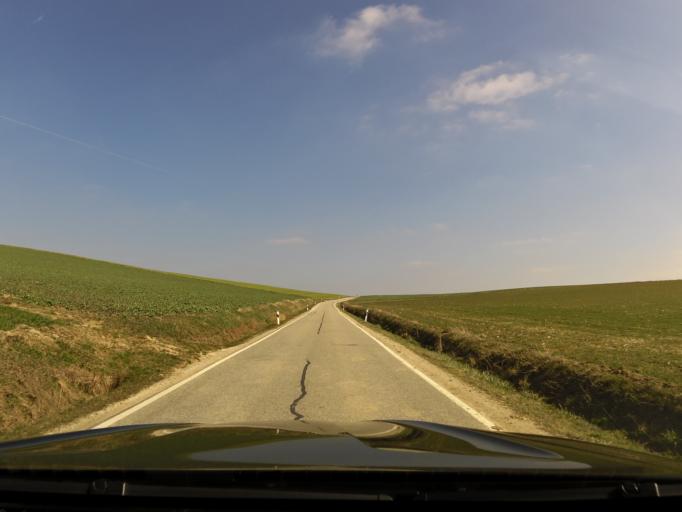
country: DE
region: Bavaria
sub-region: Lower Bavaria
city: Tiefenbach
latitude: 48.5059
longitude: 12.1170
